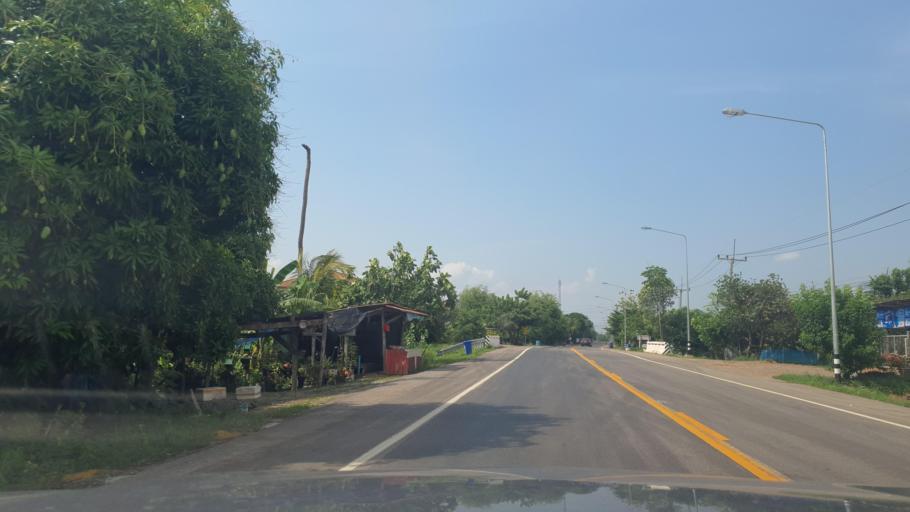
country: TH
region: Sukhothai
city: Si Samrong
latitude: 17.1609
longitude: 99.8289
